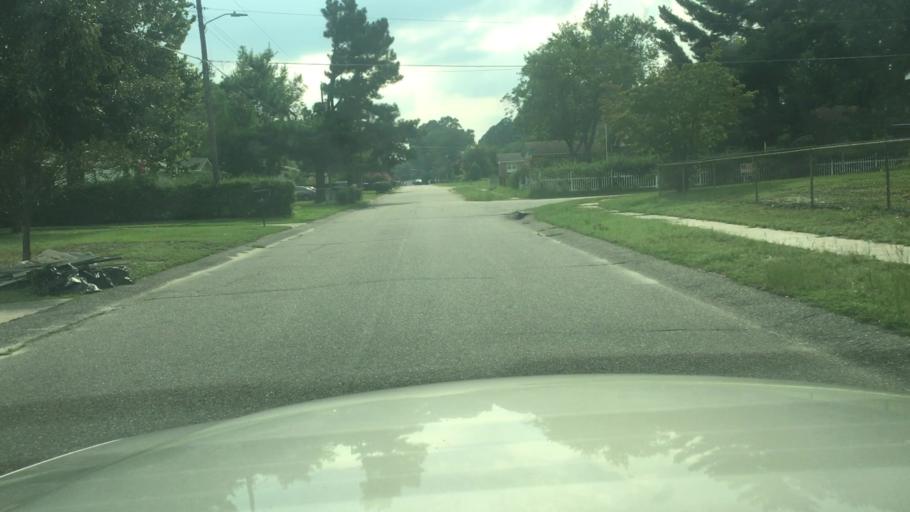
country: US
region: North Carolina
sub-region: Cumberland County
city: Fort Bragg
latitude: 35.0958
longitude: -78.9819
